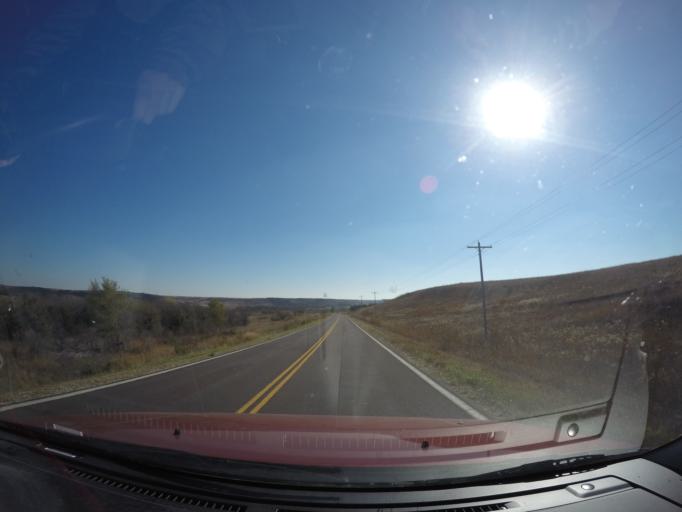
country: US
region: Kansas
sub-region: Geary County
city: Grandview Plaza
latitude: 39.0106
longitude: -96.7513
